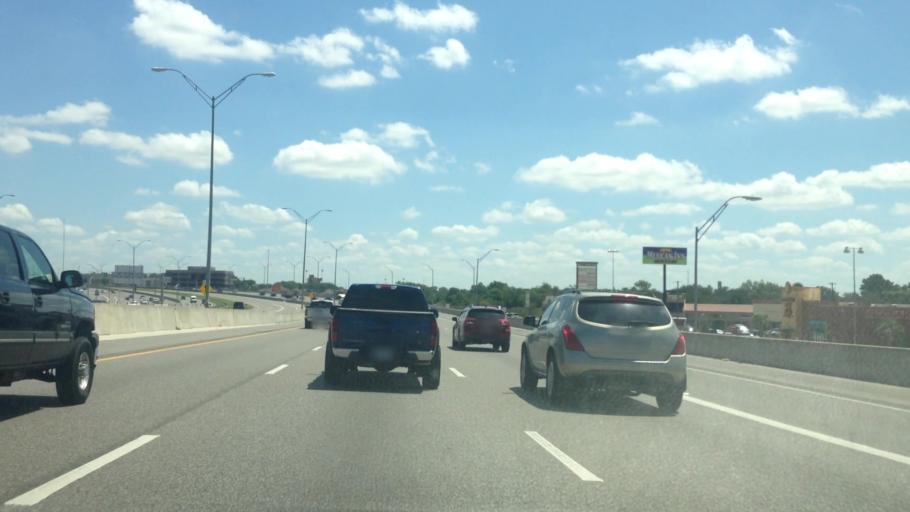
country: US
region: Texas
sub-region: Tarrant County
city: Bedford
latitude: 32.8383
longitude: -97.1496
